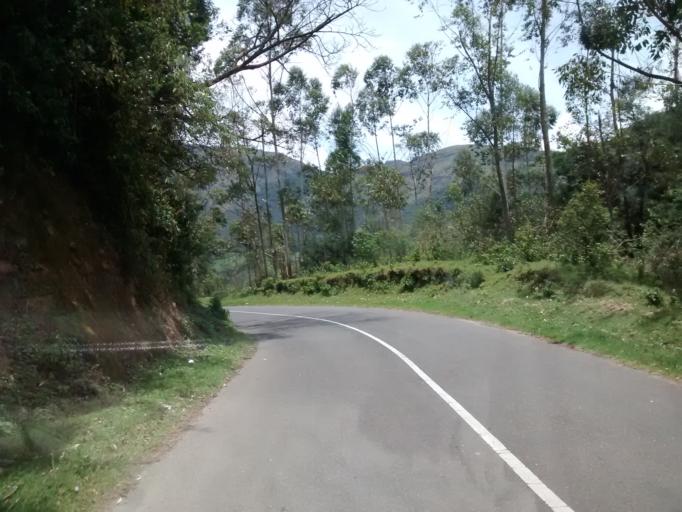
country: IN
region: Kerala
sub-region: Idukki
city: Munnar
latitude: 10.1351
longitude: 77.2057
